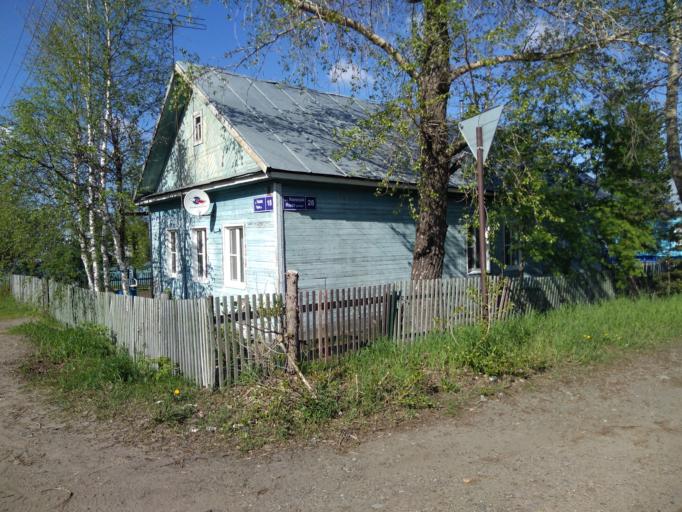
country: RU
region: Komi Republic
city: Puteyets
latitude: 65.1155
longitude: 57.1480
